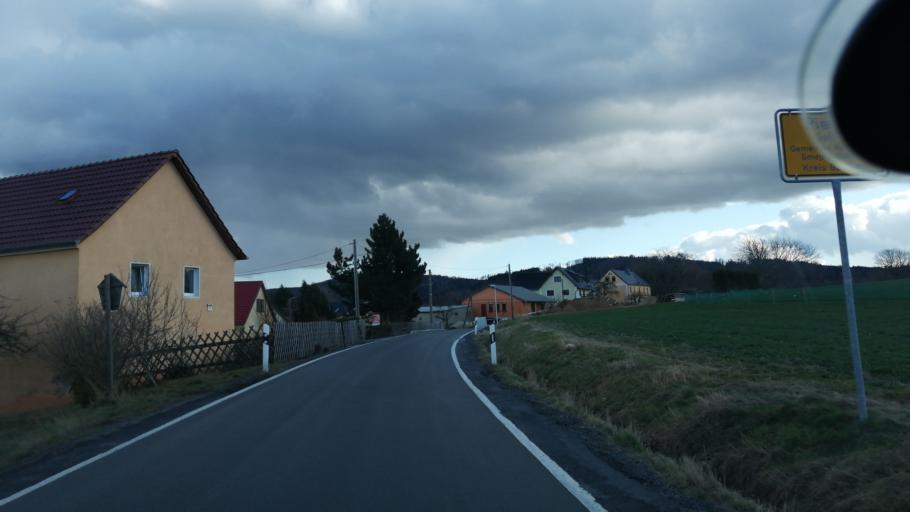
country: DE
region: Saxony
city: Kubschutz
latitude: 51.1376
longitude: 14.4868
